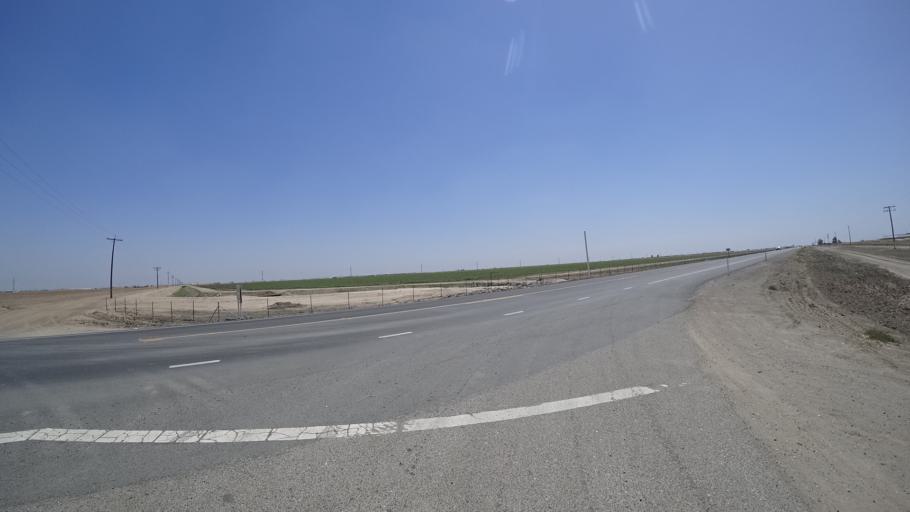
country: US
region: California
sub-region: Kings County
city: Corcoran
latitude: 36.1963
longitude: -119.6005
